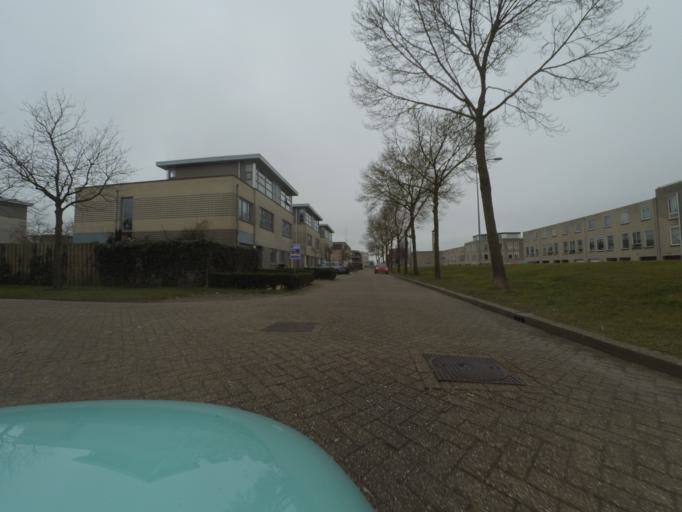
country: NL
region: Flevoland
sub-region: Gemeente Zeewolde
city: Zeewolde
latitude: 52.3341
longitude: 5.5433
